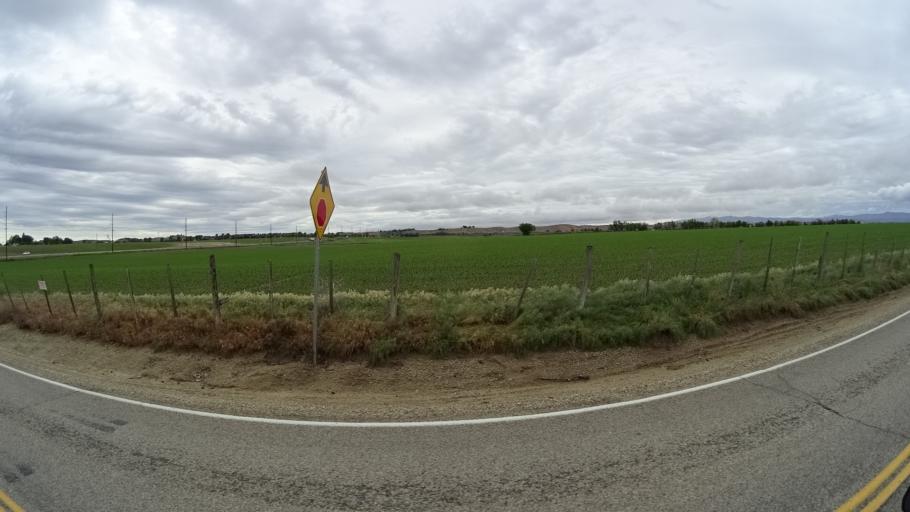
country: US
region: Idaho
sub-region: Ada County
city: Star
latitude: 43.7099
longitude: -116.4556
